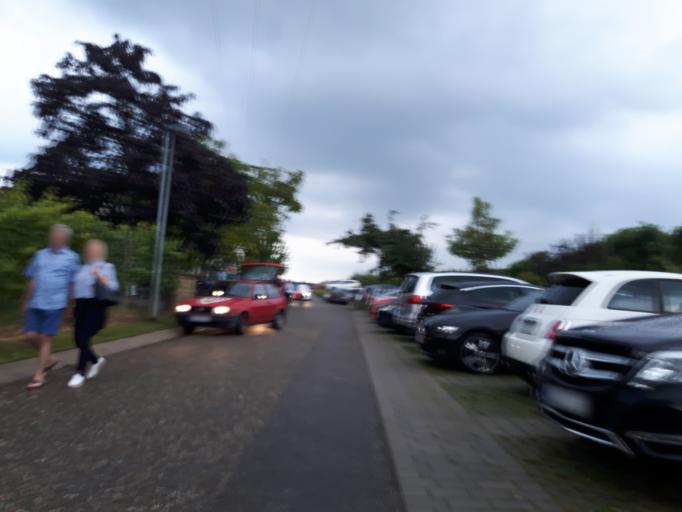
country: DE
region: Baden-Wuerttemberg
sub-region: Regierungsbezirk Stuttgart
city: Eberstadt
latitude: 49.1833
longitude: 9.3051
